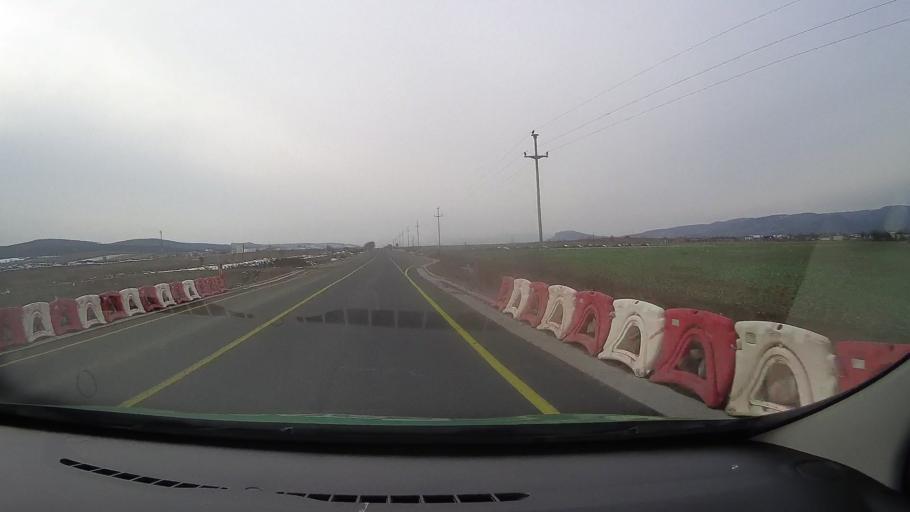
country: RO
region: Hunedoara
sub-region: Comuna Turdas
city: Turdas
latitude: 45.8408
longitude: 23.1384
